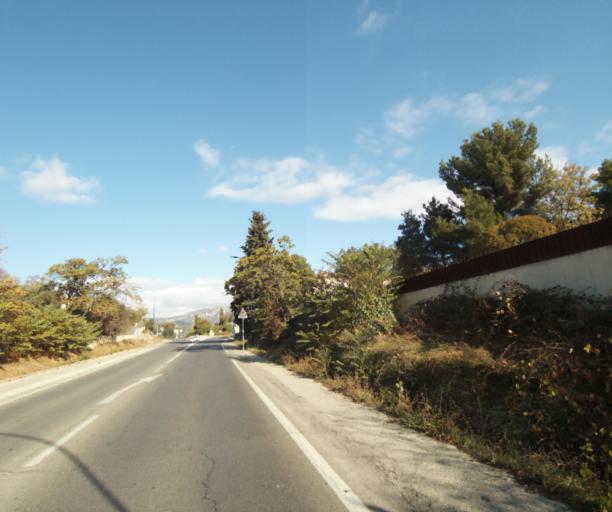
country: FR
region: Provence-Alpes-Cote d'Azur
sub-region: Departement des Bouches-du-Rhone
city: Allauch
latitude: 43.3485
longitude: 5.4874
